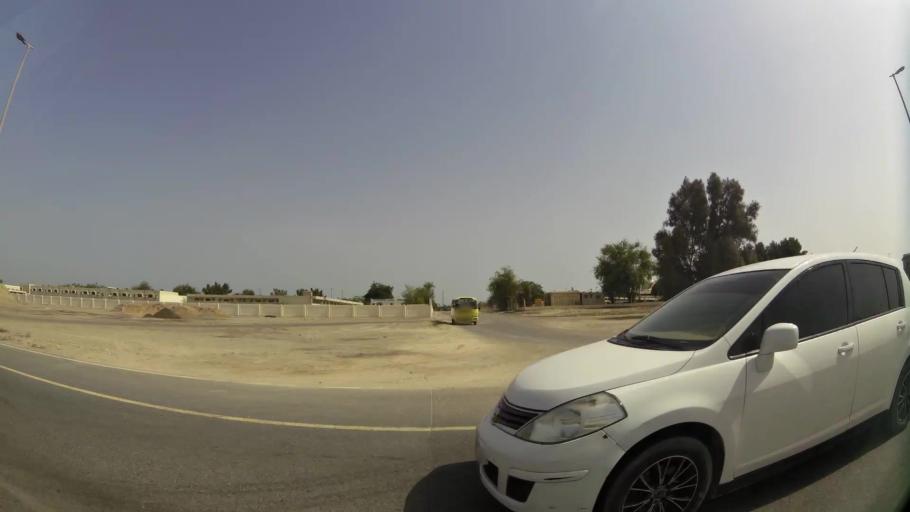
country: AE
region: Ash Shariqah
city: Sharjah
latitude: 25.3527
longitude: 55.4250
